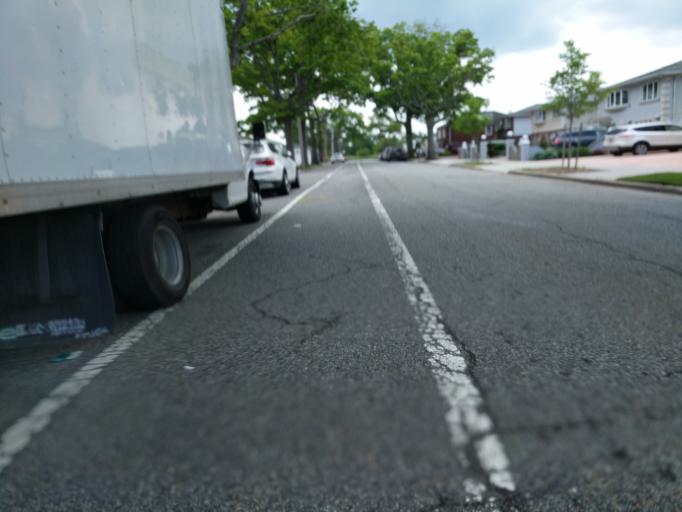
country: US
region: New York
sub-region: Queens County
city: Borough of Queens
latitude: 40.6505
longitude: -73.8397
